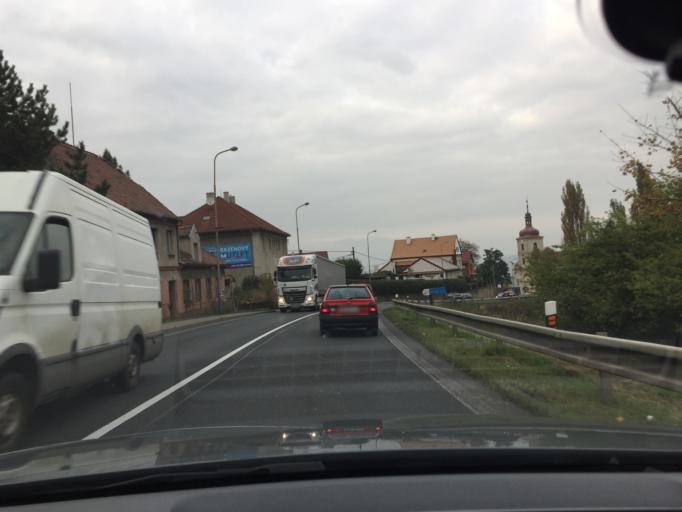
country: CZ
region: Ustecky
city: Rehlovice
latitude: 50.5775
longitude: 13.9285
